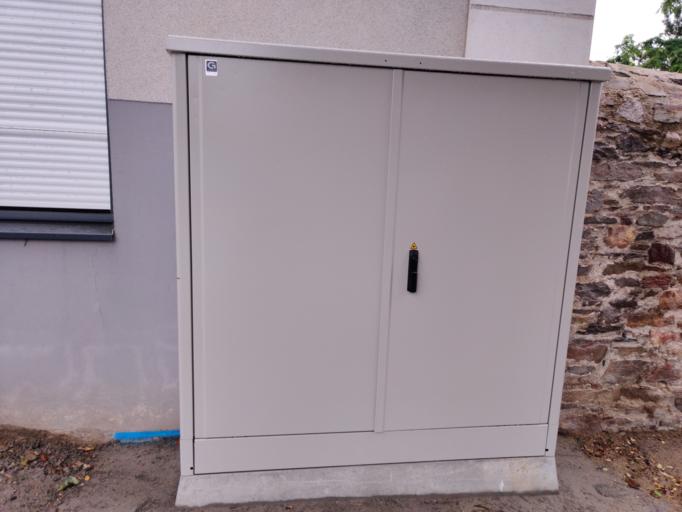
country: FR
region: Pays de la Loire
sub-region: Departement de la Vendee
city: Les Sables-d'Olonne
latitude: 46.4962
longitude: -1.7776
